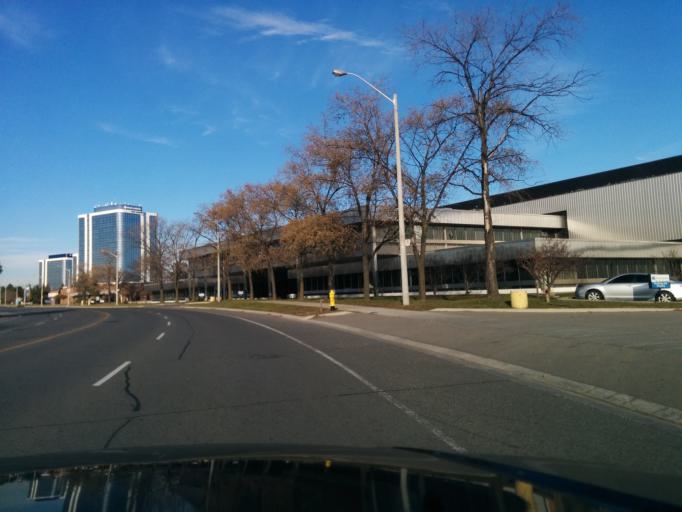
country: CA
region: Ontario
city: Etobicoke
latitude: 43.6209
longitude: -79.5606
